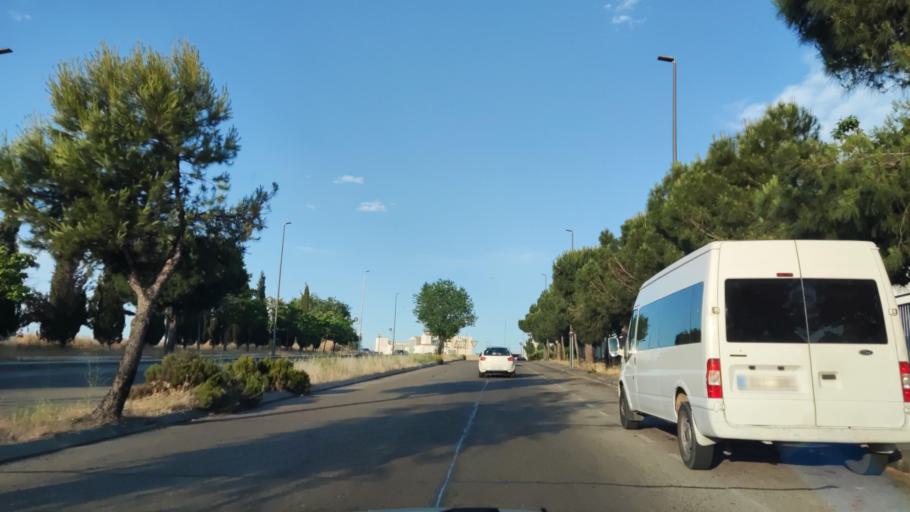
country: ES
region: Madrid
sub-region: Provincia de Madrid
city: Pinto
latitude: 40.2679
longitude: -3.6938
